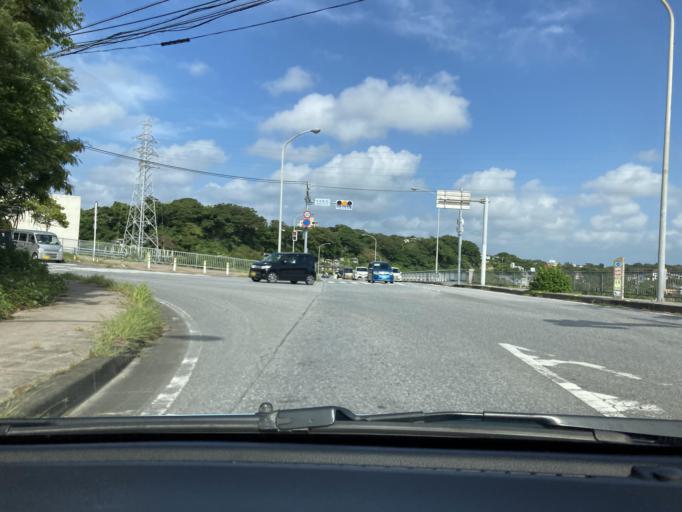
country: JP
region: Okinawa
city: Chatan
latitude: 26.2890
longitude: 127.7861
